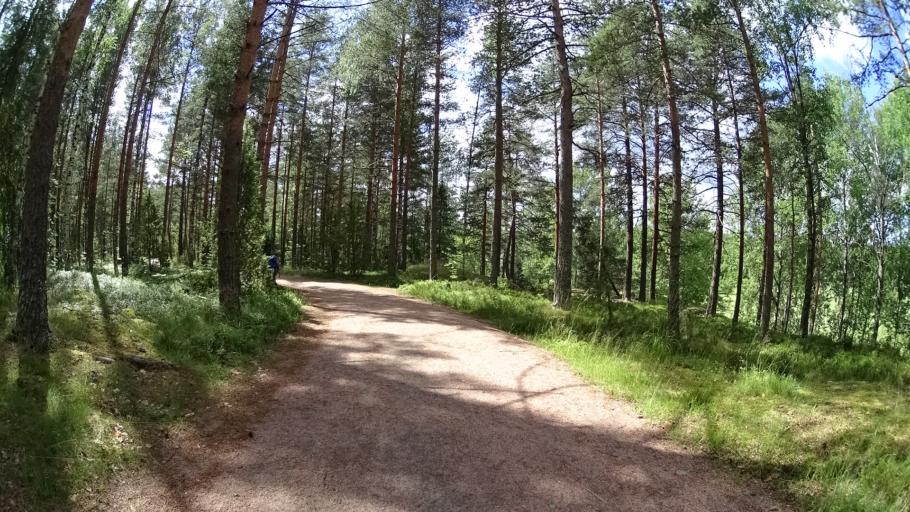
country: FI
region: Uusimaa
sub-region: Helsinki
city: Espoo
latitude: 60.3191
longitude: 24.6775
